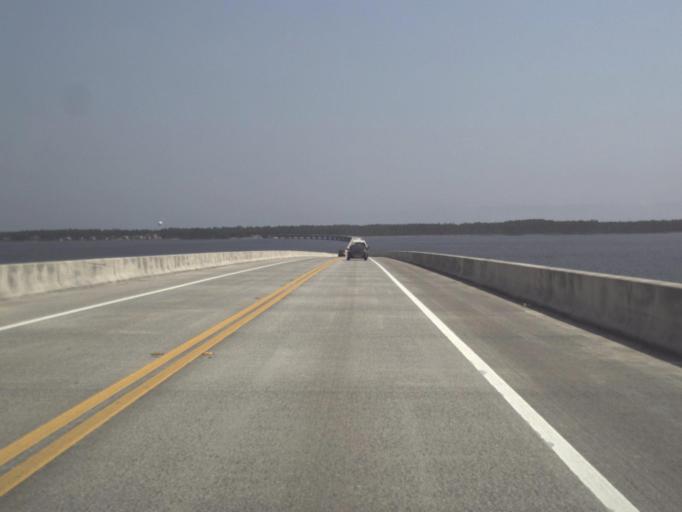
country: US
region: Florida
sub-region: Santa Rosa County
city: Oriole Beach
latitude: 30.4154
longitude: -87.0876
